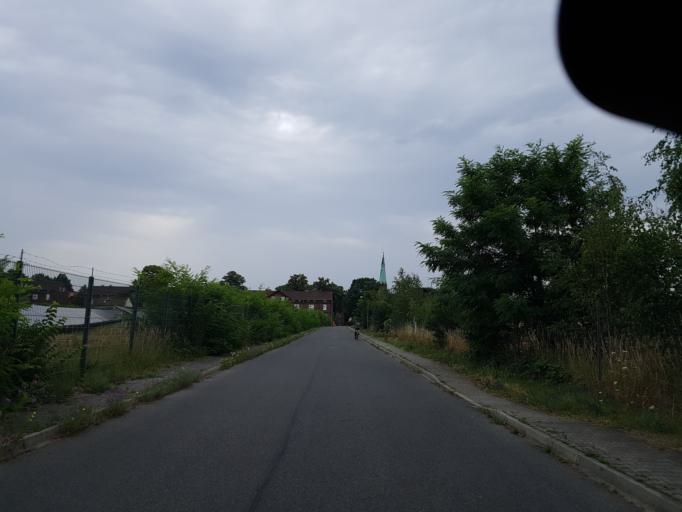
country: DE
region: Brandenburg
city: Schipkau
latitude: 51.5629
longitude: 13.8880
